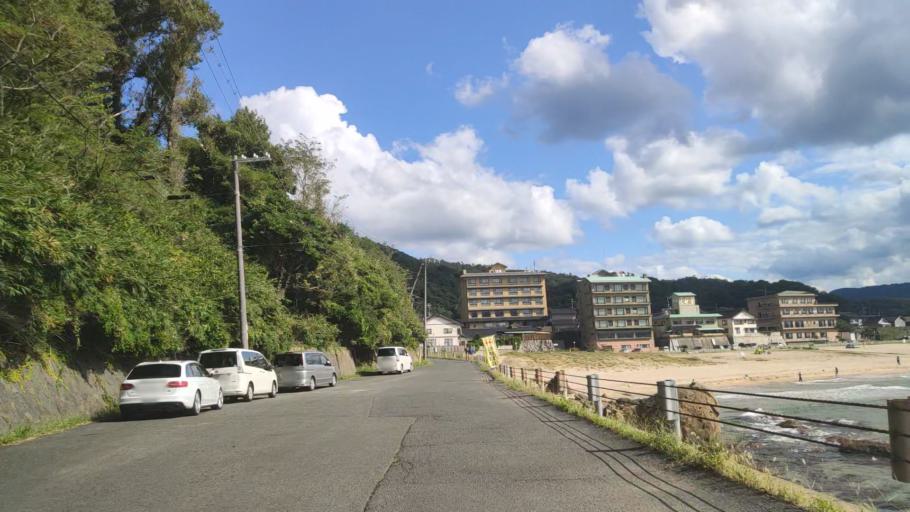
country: JP
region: Hyogo
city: Toyooka
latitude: 35.6700
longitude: 134.9666
